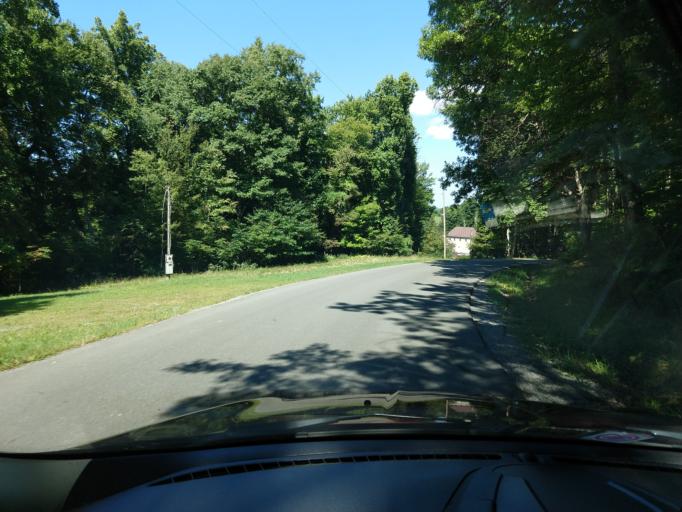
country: US
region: West Virginia
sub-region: Nicholas County
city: Craigsville
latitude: 38.2748
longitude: -80.7155
